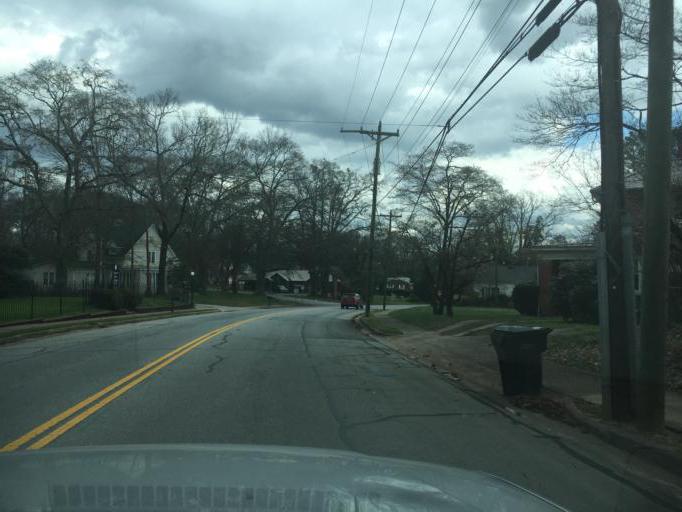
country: US
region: South Carolina
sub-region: Oconee County
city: Westminster
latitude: 34.6702
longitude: -83.0991
